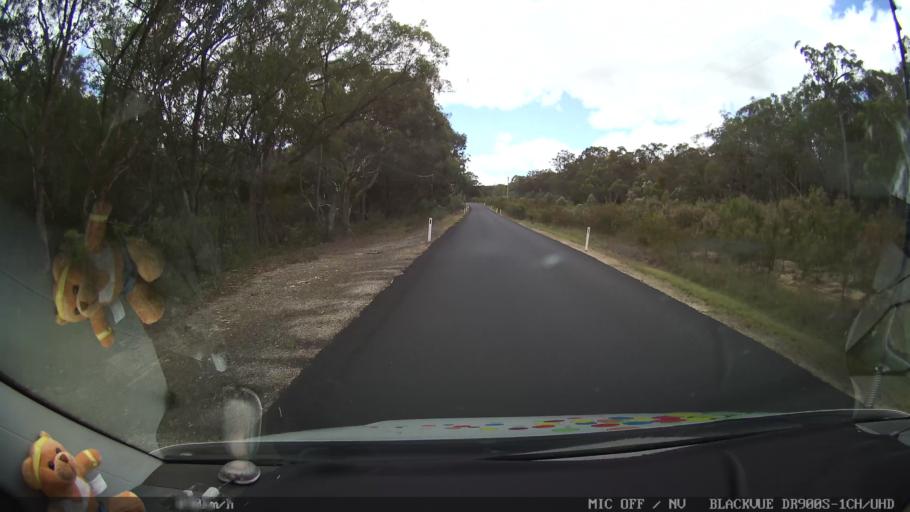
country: AU
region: New South Wales
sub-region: Glen Innes Severn
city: Glen Innes
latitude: -29.4388
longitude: 151.6253
